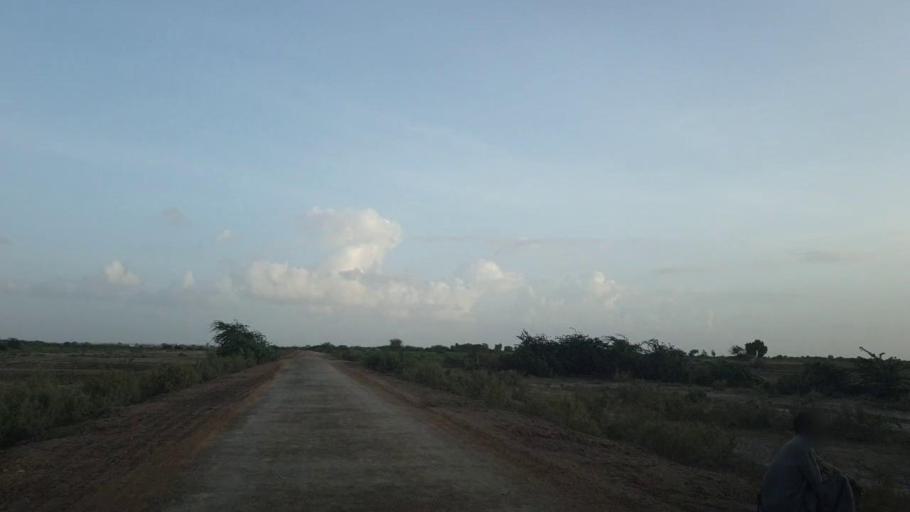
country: PK
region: Sindh
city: Kadhan
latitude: 24.5622
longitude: 69.1215
